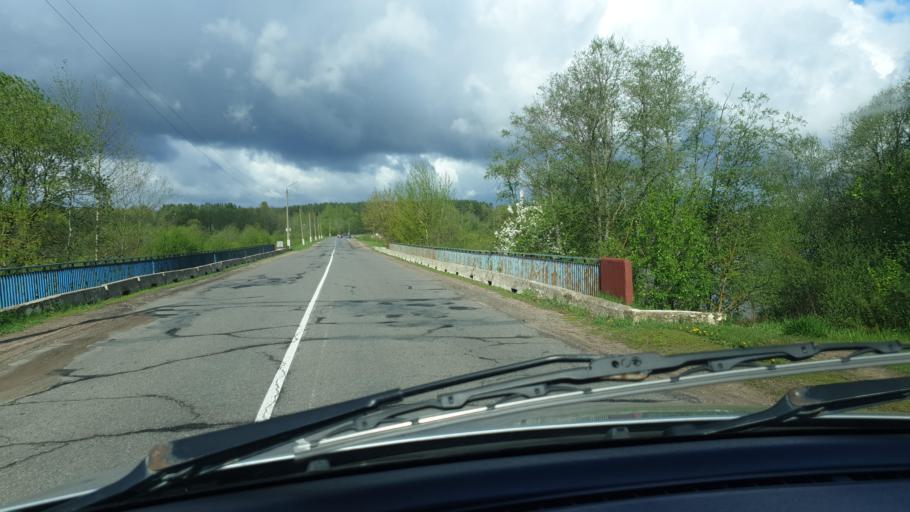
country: BY
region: Vitebsk
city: Lyepyel'
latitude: 54.8768
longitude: 28.6689
